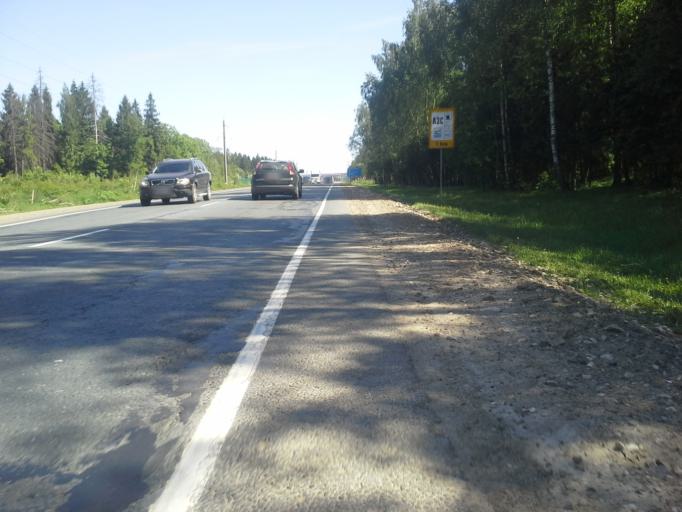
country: RU
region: Moskovskaya
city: Troitsk
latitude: 55.4265
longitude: 37.1735
